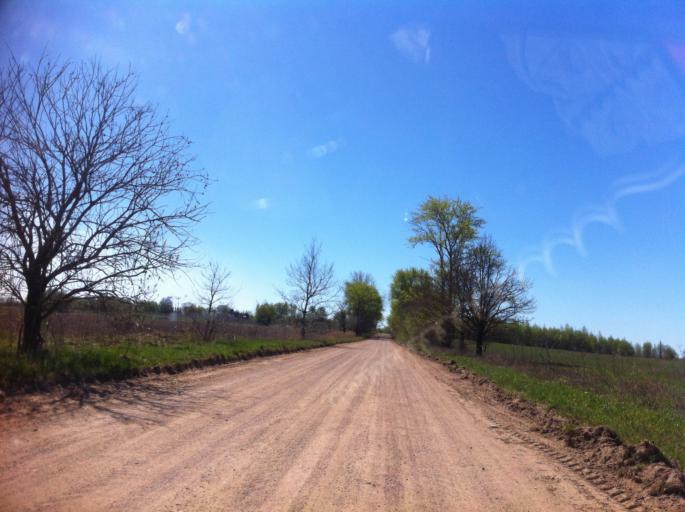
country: RU
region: Pskov
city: Izborsk
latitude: 57.7935
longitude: 27.9635
